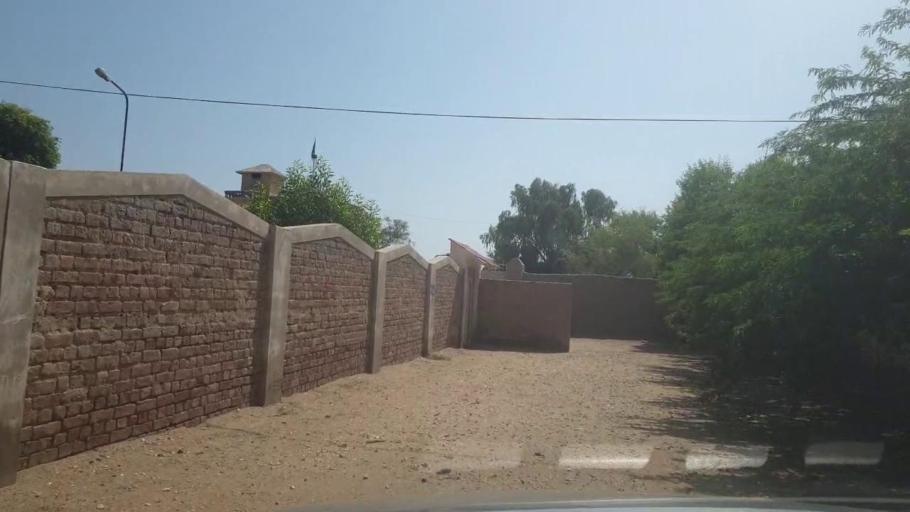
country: PK
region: Sindh
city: Rohri
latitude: 27.4063
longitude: 69.0813
